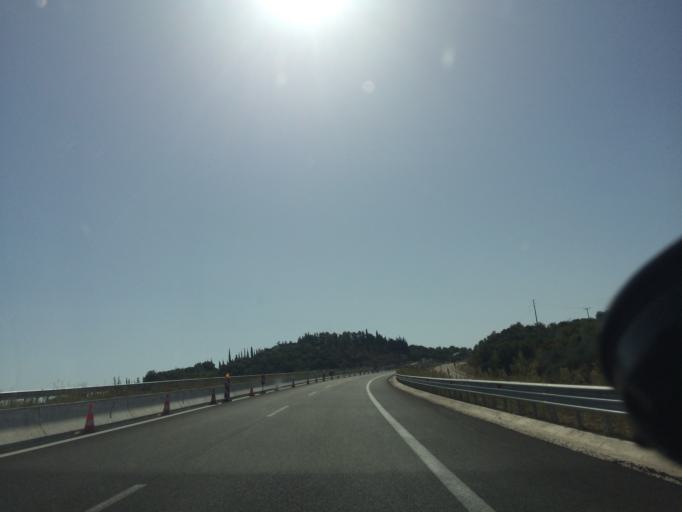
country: GR
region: Thessaly
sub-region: Nomos Larisis
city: Pyrgetos
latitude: 39.9668
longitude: 22.6432
